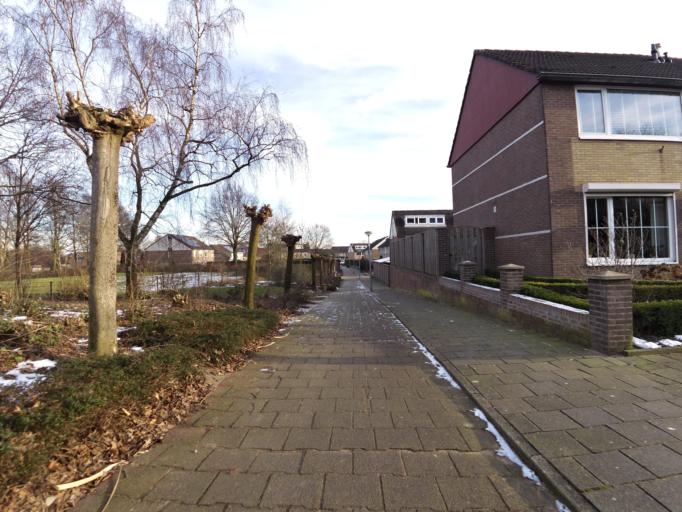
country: NL
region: Gelderland
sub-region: Gemeente Montferland
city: s-Heerenberg
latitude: 51.8819
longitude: 6.2601
